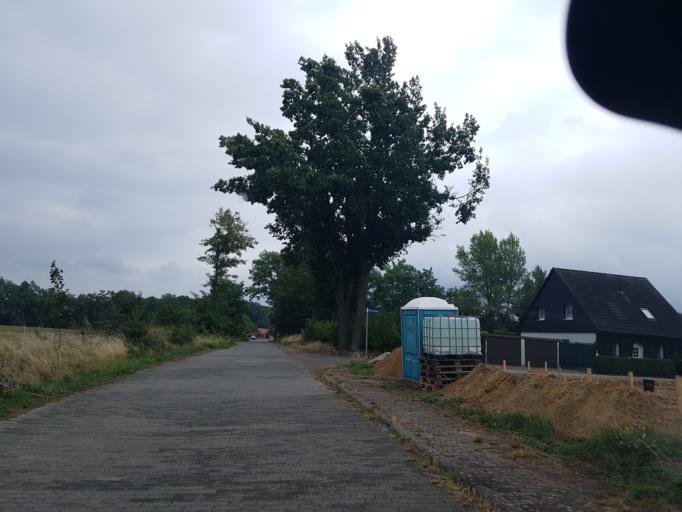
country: DE
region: Saxony-Anhalt
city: Loburg
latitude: 52.2446
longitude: 12.0464
